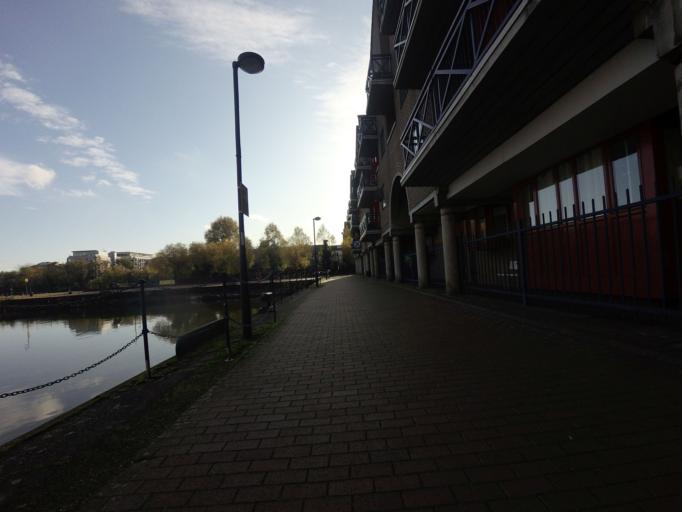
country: GB
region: England
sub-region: Greater London
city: Bethnal Green
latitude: 51.5087
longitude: -0.0547
